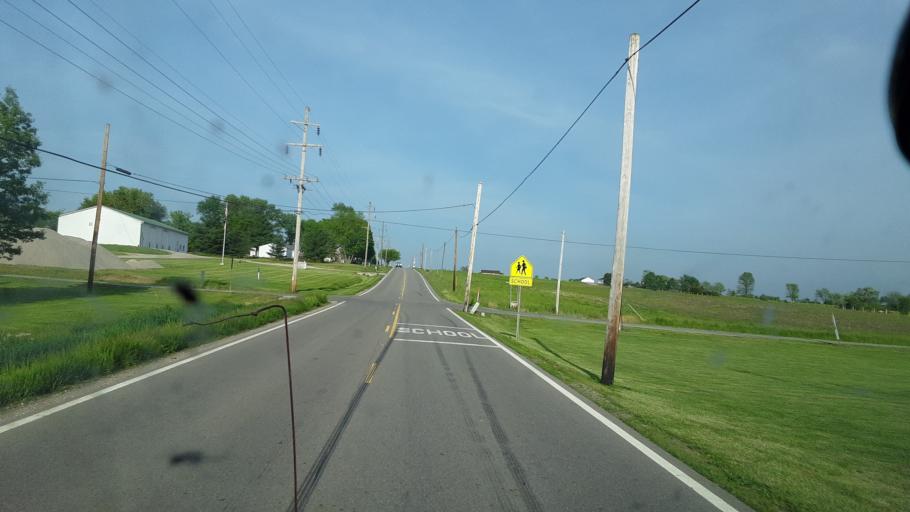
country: US
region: Ohio
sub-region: Ross County
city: Kingston
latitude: 39.5143
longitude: -82.7921
